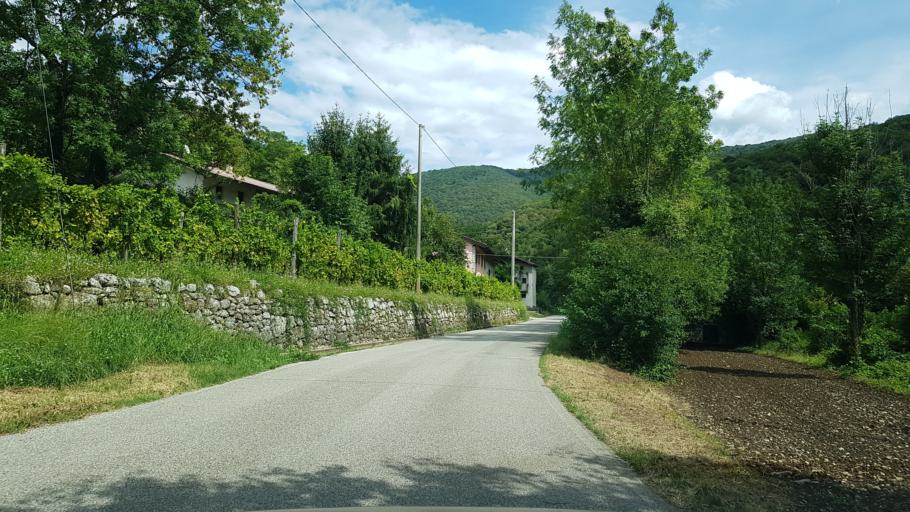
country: IT
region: Friuli Venezia Giulia
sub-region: Provincia di Udine
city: Prepotto
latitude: 46.0642
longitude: 13.5174
